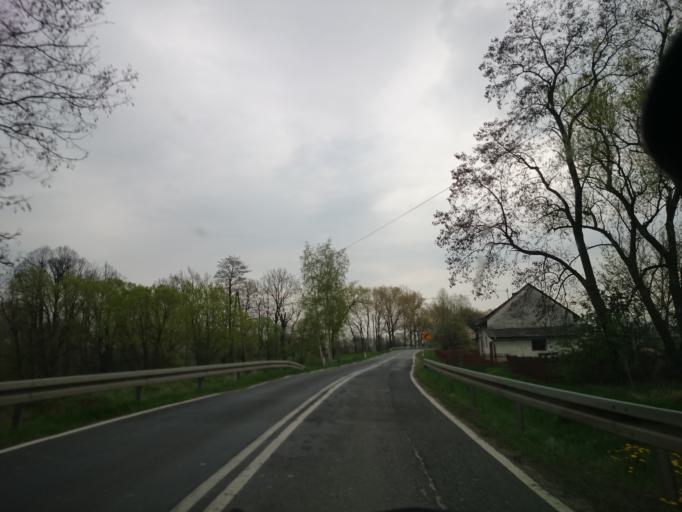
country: PL
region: Opole Voivodeship
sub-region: Powiat prudnicki
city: Moszczanka
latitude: 50.3277
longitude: 17.4782
